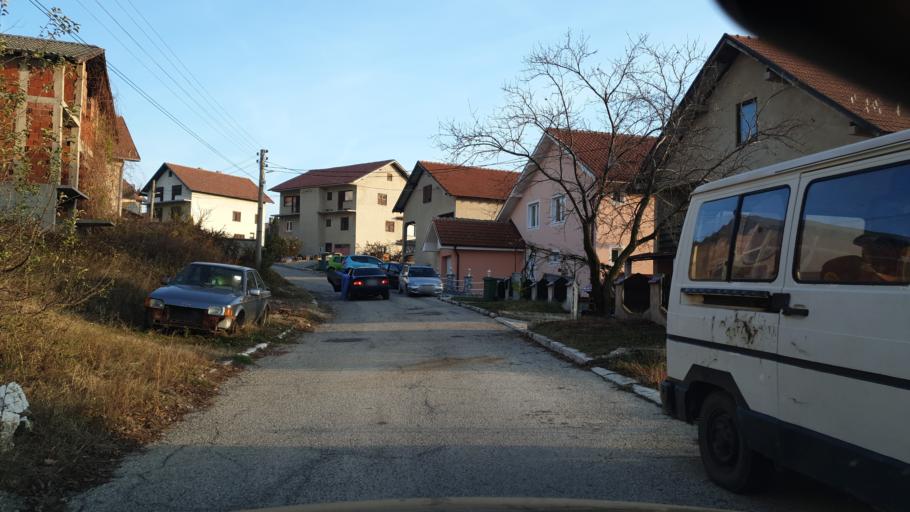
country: RS
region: Central Serbia
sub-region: Borski Okrug
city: Bor
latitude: 44.0589
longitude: 22.0805
